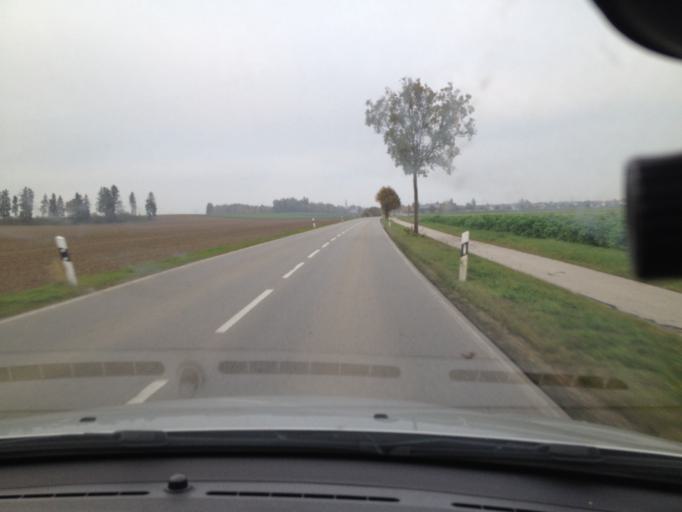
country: DE
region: Bavaria
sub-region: Swabia
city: Kleinaitingen
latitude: 48.2073
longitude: 10.8333
